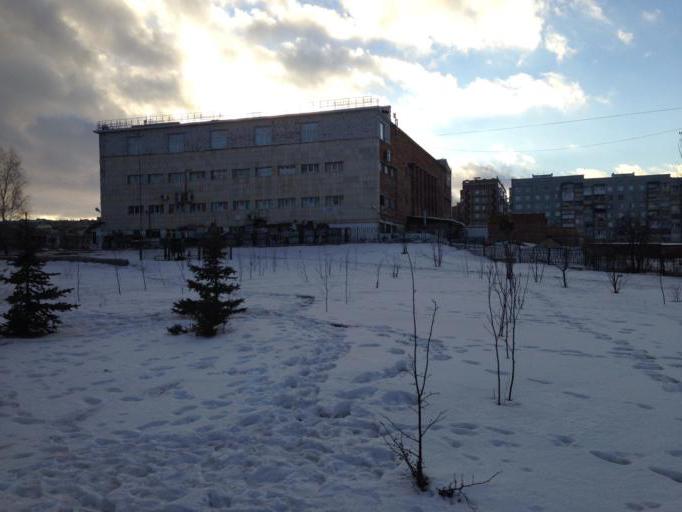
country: RU
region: Bashkortostan
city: Oktyabr'skiy
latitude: 54.4824
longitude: 53.5266
